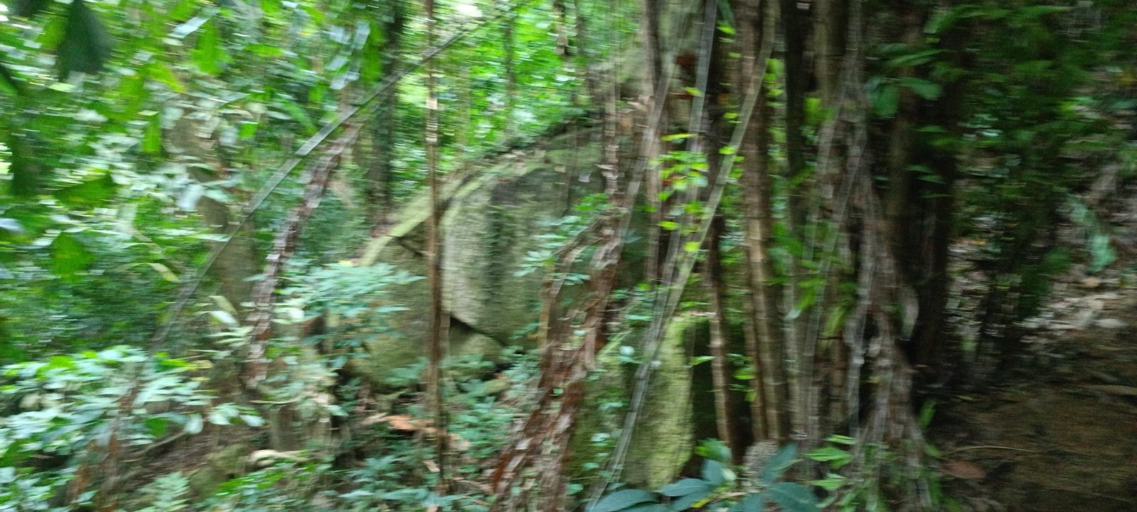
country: MY
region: Penang
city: Kampung Sungai Ara
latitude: 5.3460
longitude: 100.2832
